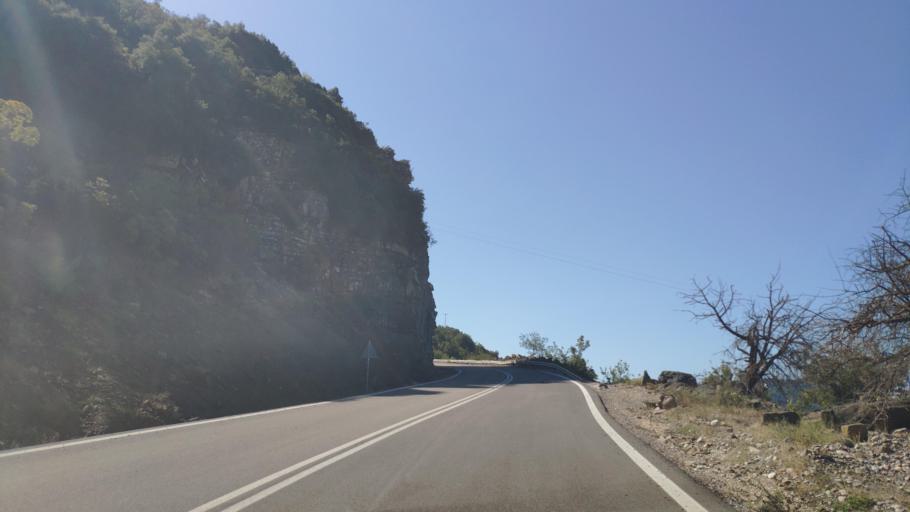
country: GR
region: West Greece
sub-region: Nomos Aitolias kai Akarnanias
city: Sardinia
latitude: 38.9243
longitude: 21.4200
